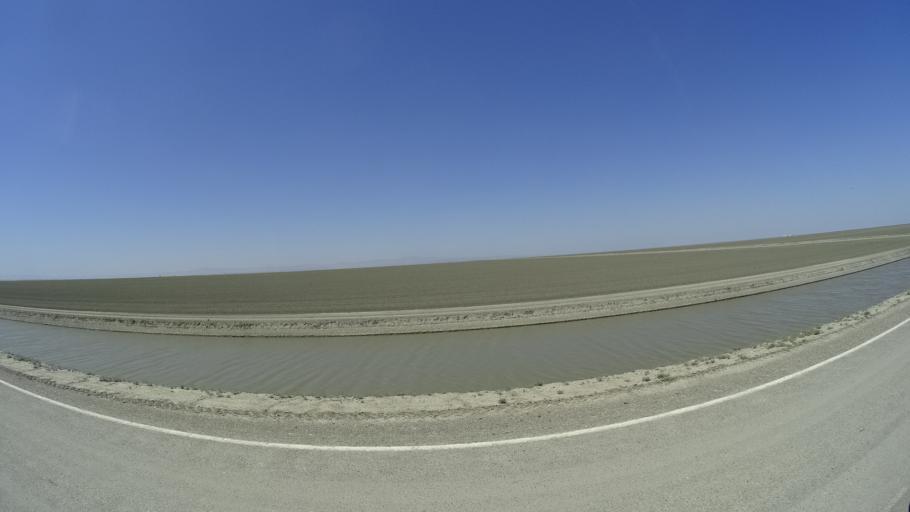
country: US
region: California
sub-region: Kings County
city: Corcoran
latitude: 35.9769
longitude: -119.6431
